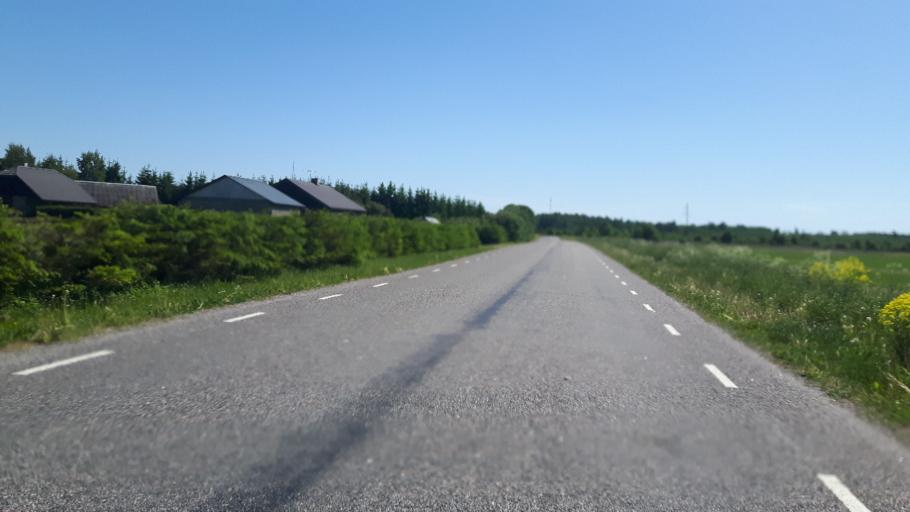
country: EE
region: Raplamaa
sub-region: Kohila vald
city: Kohila
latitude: 59.1874
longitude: 24.7119
